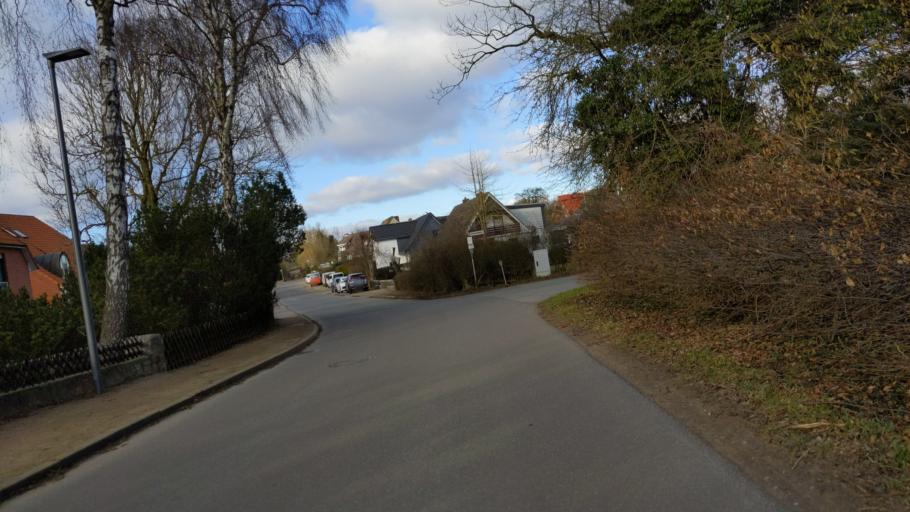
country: DE
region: Schleswig-Holstein
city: Susel
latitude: 54.0829
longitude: 10.7155
